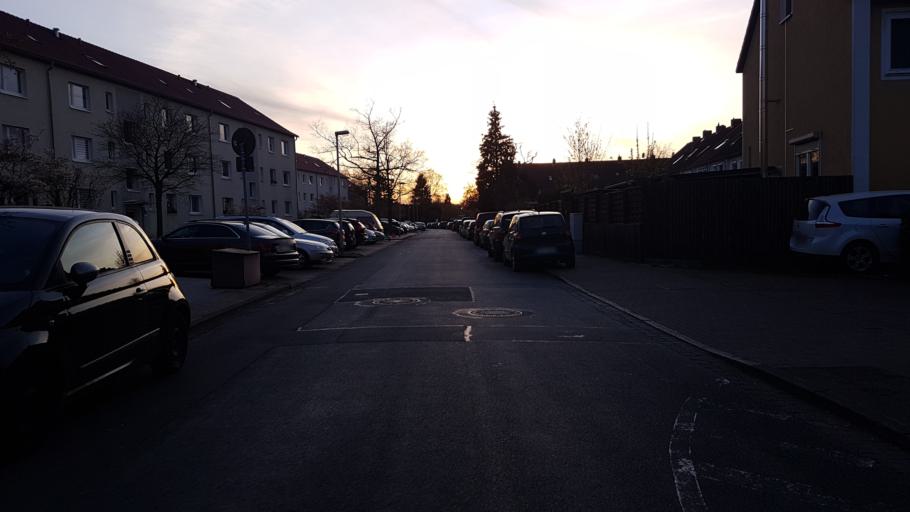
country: DE
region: Lower Saxony
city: Isernhagen Farster Bauerschaft
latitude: 52.4214
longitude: 9.8037
